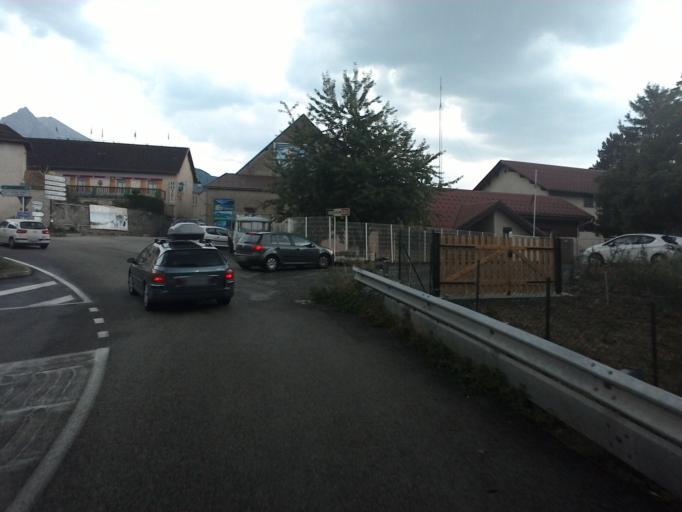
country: FR
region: Rhone-Alpes
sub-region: Departement de l'Isere
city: La Mure
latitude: 44.8201
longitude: 5.9462
